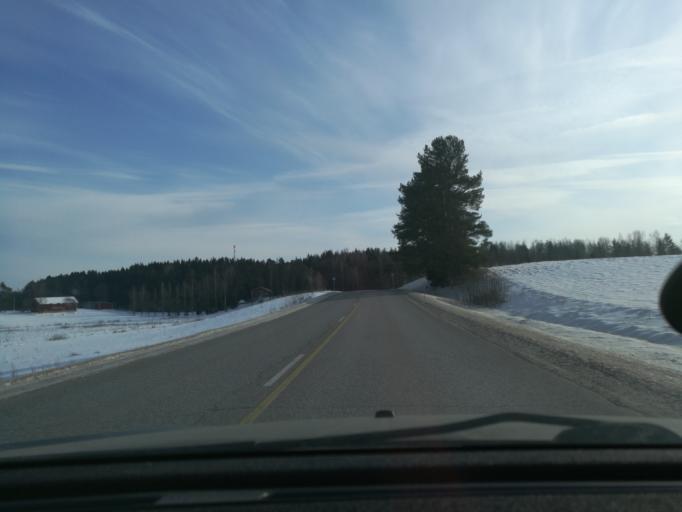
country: FI
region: Uusimaa
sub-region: Helsinki
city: Saukkola
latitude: 60.3914
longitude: 24.0758
